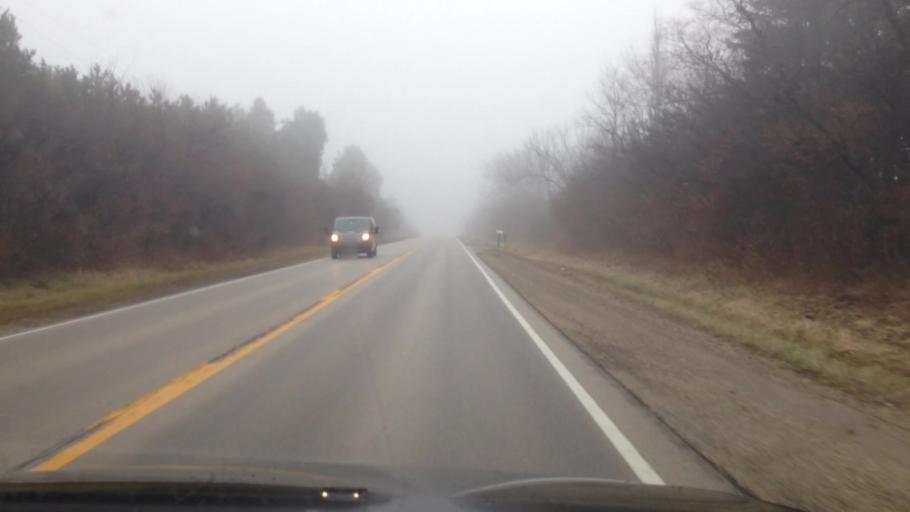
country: US
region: Illinois
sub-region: McHenry County
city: Woodstock
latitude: 42.3809
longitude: -88.4432
